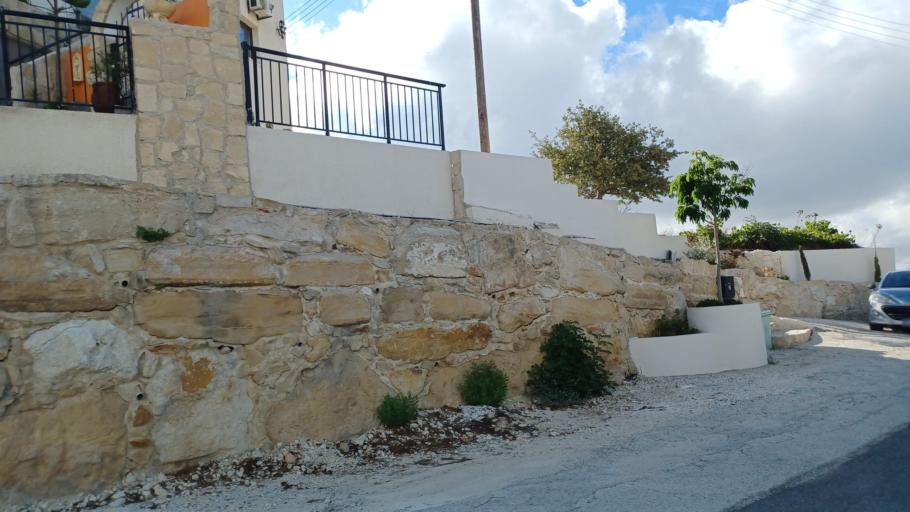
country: CY
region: Pafos
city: Tala
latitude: 34.8569
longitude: 32.4509
